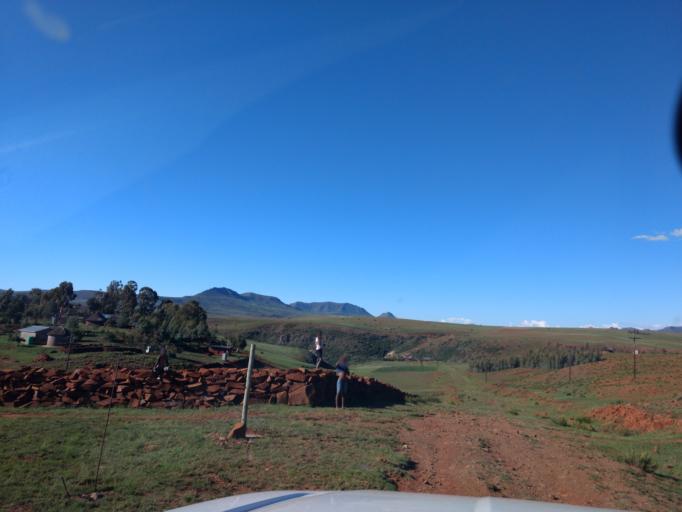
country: LS
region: Berea
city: Teyateyaneng
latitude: -29.3678
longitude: 27.7850
